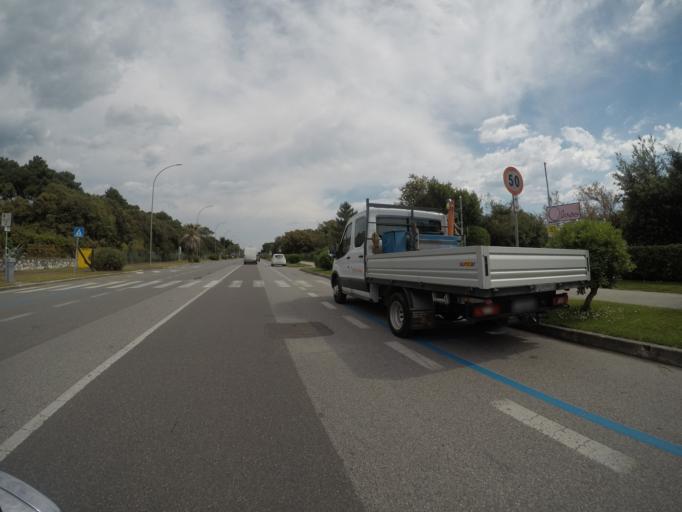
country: IT
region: Tuscany
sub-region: Provincia di Massa-Carrara
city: Capanne-Prato-Cinquale
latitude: 43.9880
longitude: 10.1297
